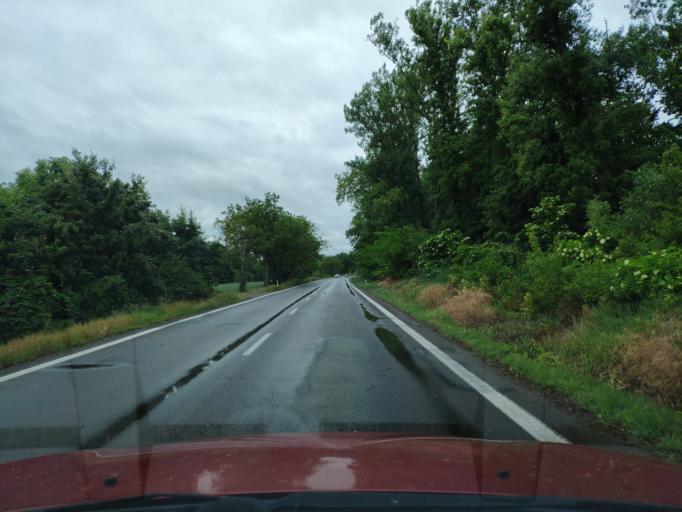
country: HU
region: Borsod-Abauj-Zemplen
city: Karcsa
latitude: 48.3901
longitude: 21.7790
